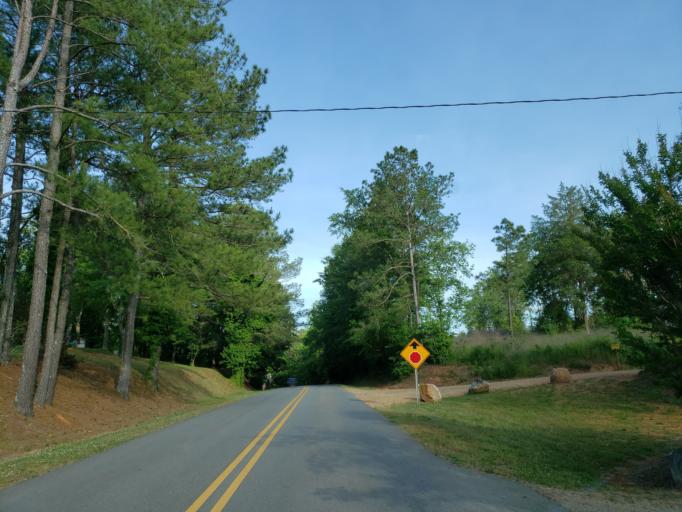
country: US
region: Georgia
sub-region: Carroll County
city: Bowdon
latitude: 33.4914
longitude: -85.3073
